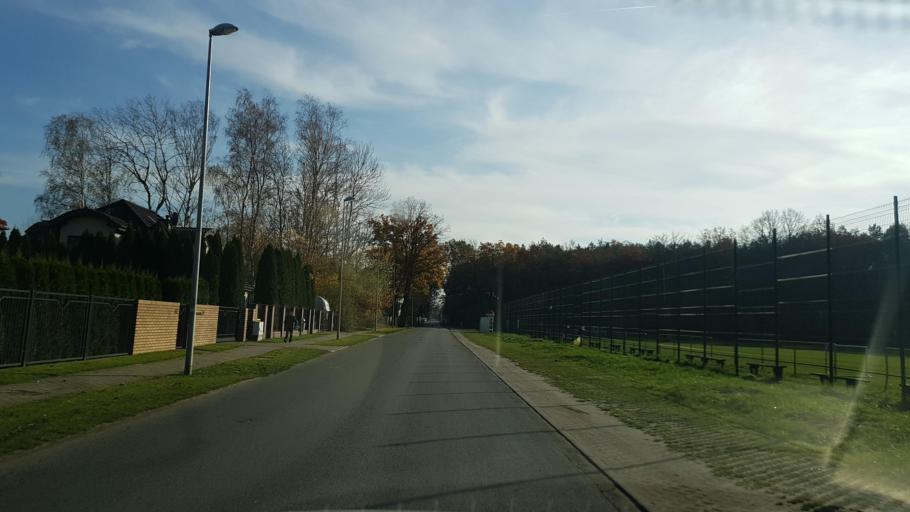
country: PL
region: West Pomeranian Voivodeship
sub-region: Powiat policki
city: Dobra
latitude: 53.4911
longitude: 14.3759
